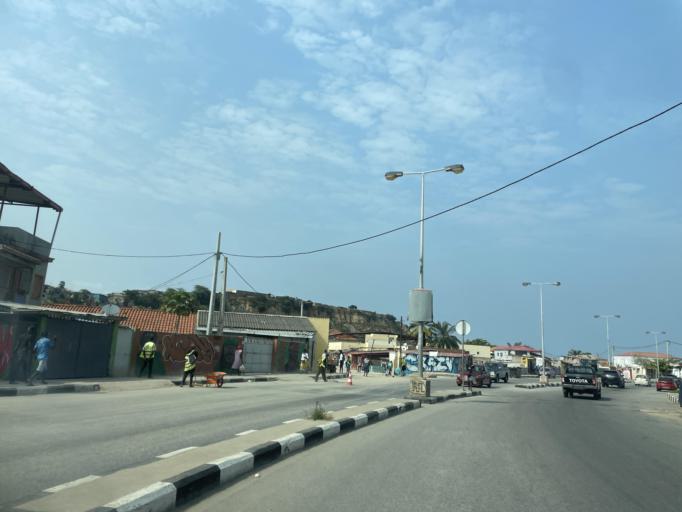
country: AO
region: Luanda
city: Luanda
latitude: -8.8300
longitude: 13.2165
